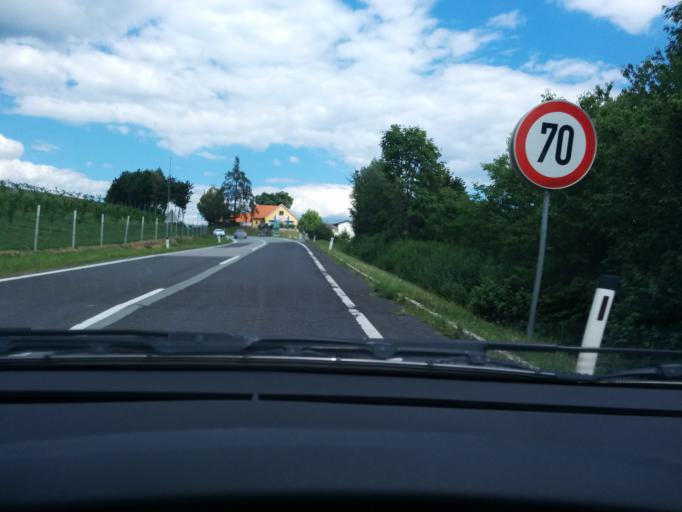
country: AT
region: Styria
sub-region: Politischer Bezirk Weiz
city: Nitscha
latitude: 47.1306
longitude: 15.7274
